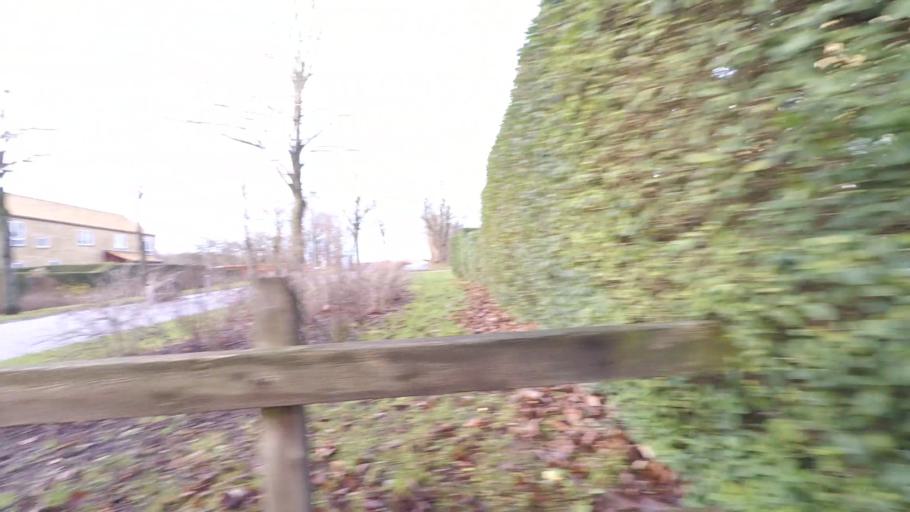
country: DK
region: Central Jutland
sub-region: Arhus Kommune
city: Marslet
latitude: 56.1064
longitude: 10.1687
